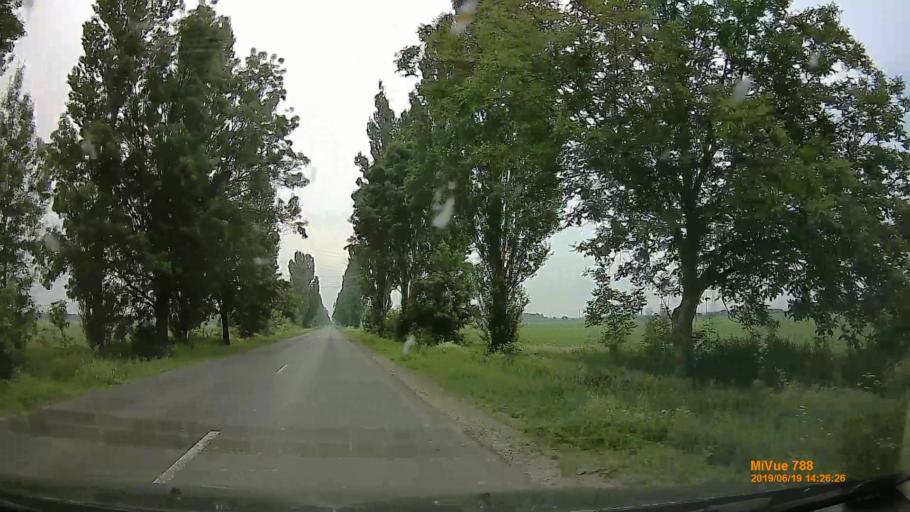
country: HU
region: Baranya
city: Szigetvar
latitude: 46.0313
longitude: 17.7799
